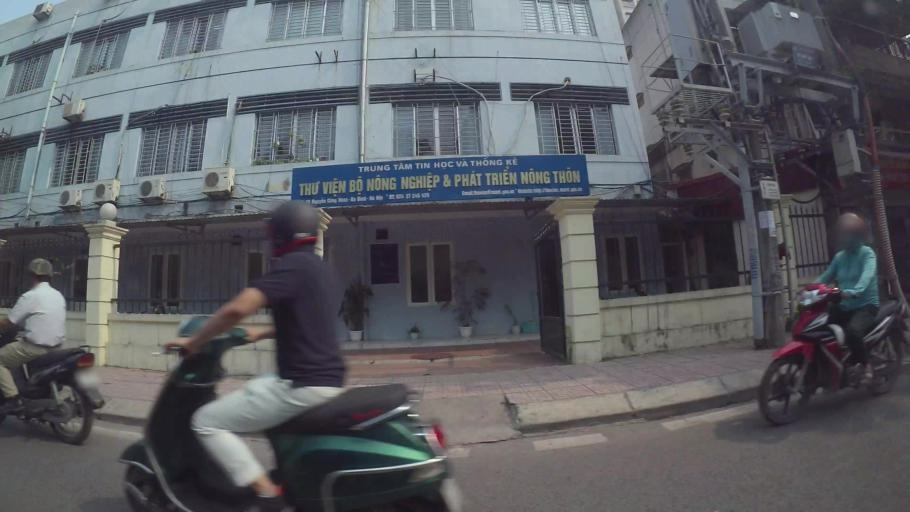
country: VN
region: Ha Noi
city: Dong Da
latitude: 21.0272
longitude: 105.8165
